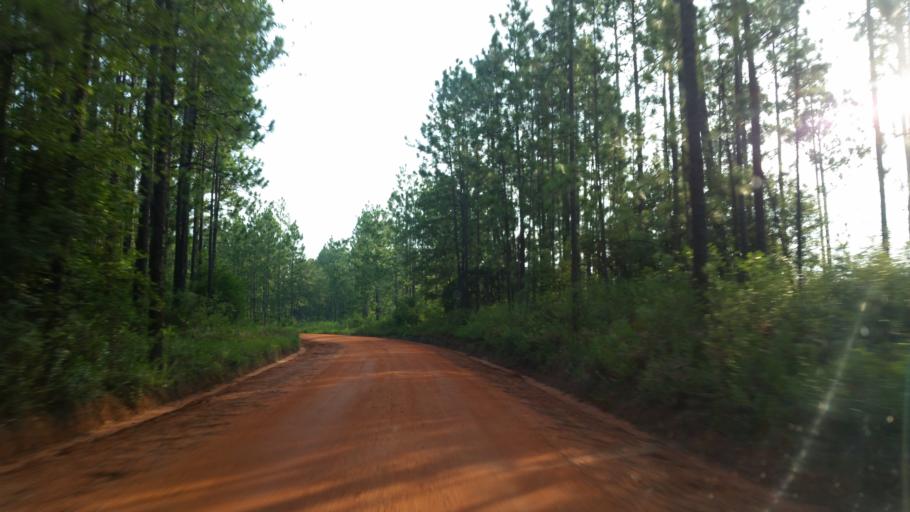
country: US
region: Alabama
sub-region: Escambia County
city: Atmore
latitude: 30.9295
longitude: -87.5704
